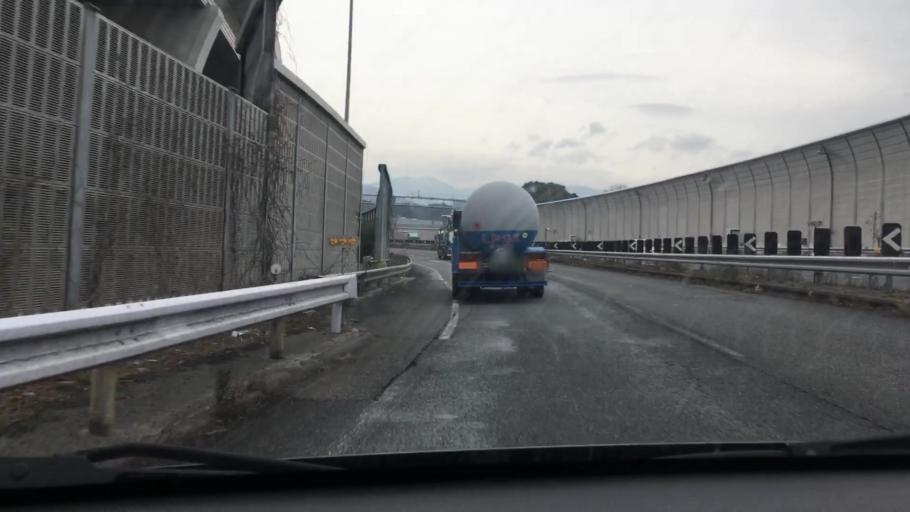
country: JP
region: Mie
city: Kameyama
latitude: 34.8523
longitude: 136.4172
